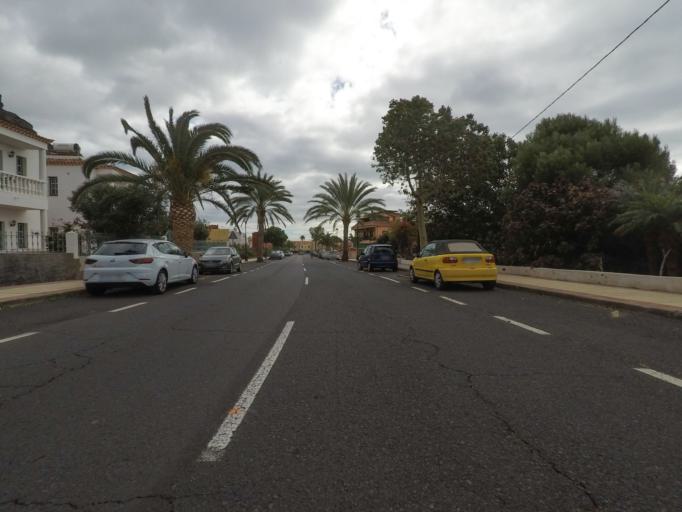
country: ES
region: Canary Islands
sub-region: Provincia de Santa Cruz de Tenerife
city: Alajero
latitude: 28.0898
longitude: -17.3364
